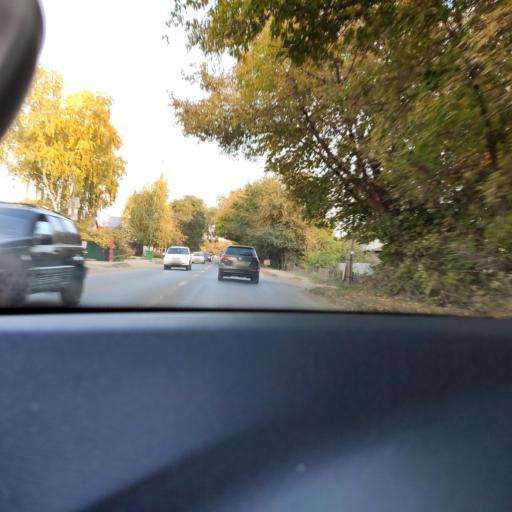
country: RU
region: Samara
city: Smyshlyayevka
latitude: 53.2514
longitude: 50.3560
